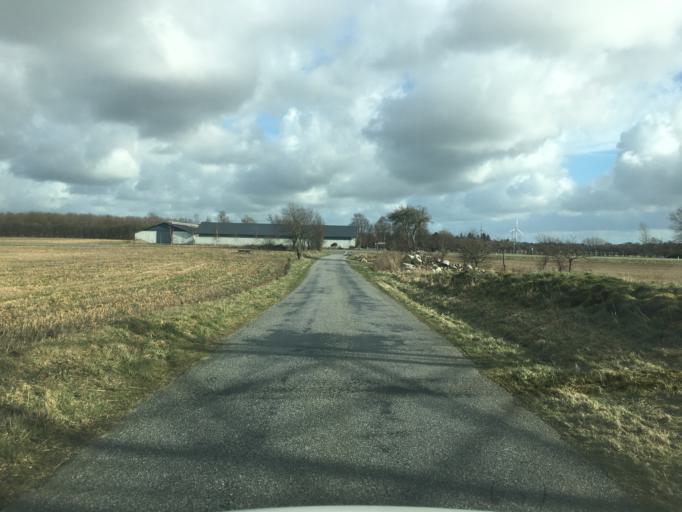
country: DK
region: South Denmark
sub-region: Aabenraa Kommune
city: Krusa
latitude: 54.9133
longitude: 9.3755
